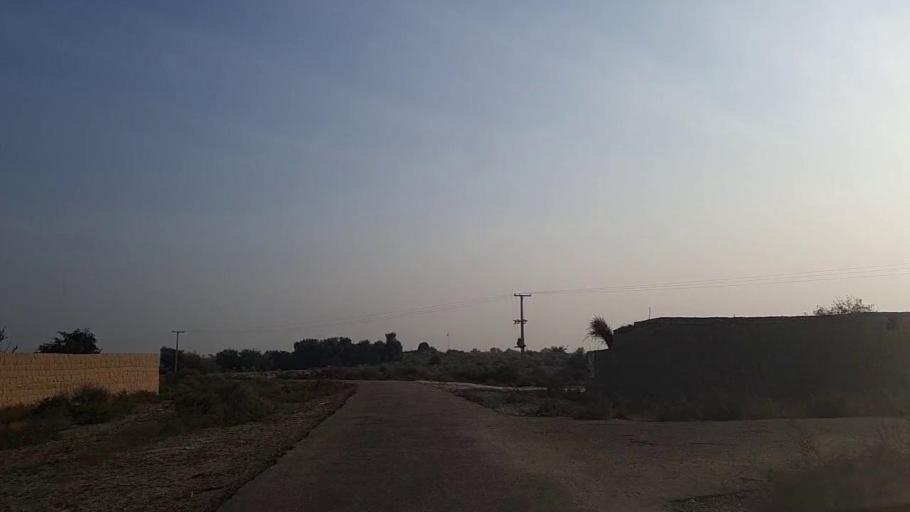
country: PK
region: Sindh
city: Jam Sahib
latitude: 26.4344
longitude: 68.5931
